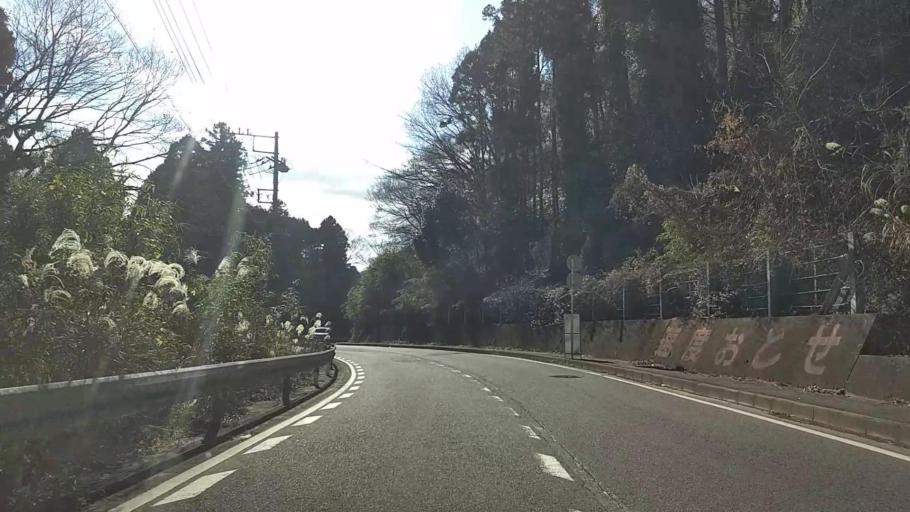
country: JP
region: Kanagawa
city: Atsugi
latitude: 35.4617
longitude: 139.2905
